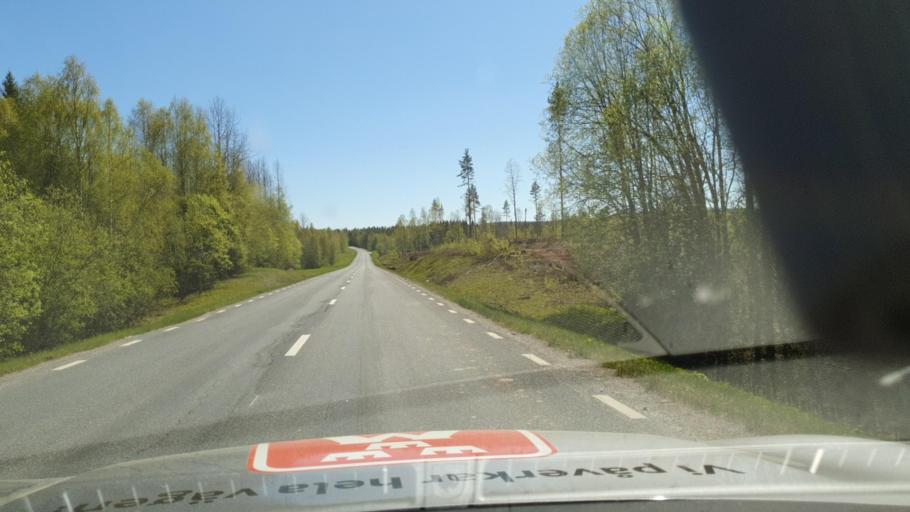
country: SE
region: Vaesternorrland
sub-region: OErnskoeldsviks Kommun
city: Ornskoldsvik
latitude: 63.5739
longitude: 18.5487
